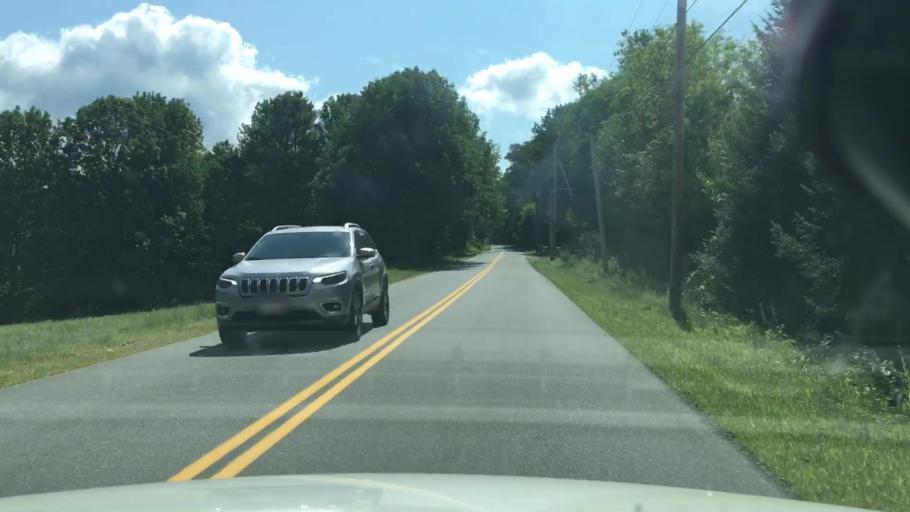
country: US
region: Maine
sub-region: Somerset County
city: Skowhegan
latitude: 44.7354
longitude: -69.7106
